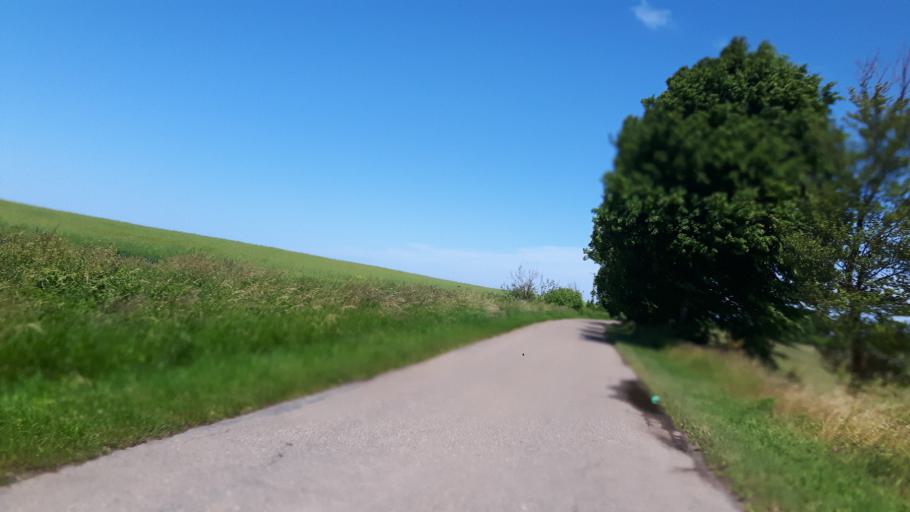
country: PL
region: West Pomeranian Voivodeship
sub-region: Powiat gryficki
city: Mrzezyno
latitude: 54.1105
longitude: 15.3066
